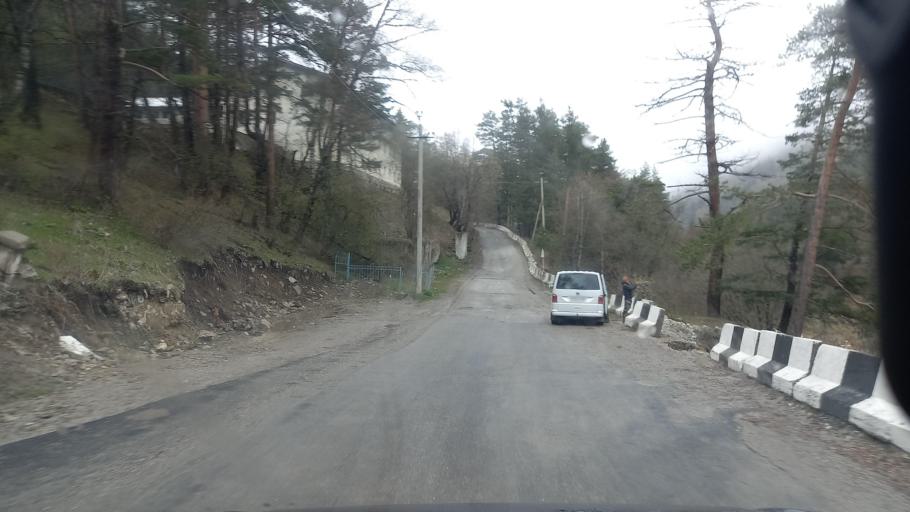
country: RU
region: Kabardino-Balkariya
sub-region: El'brusskiy Rayon
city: El'brus
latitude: 43.2293
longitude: 42.6541
